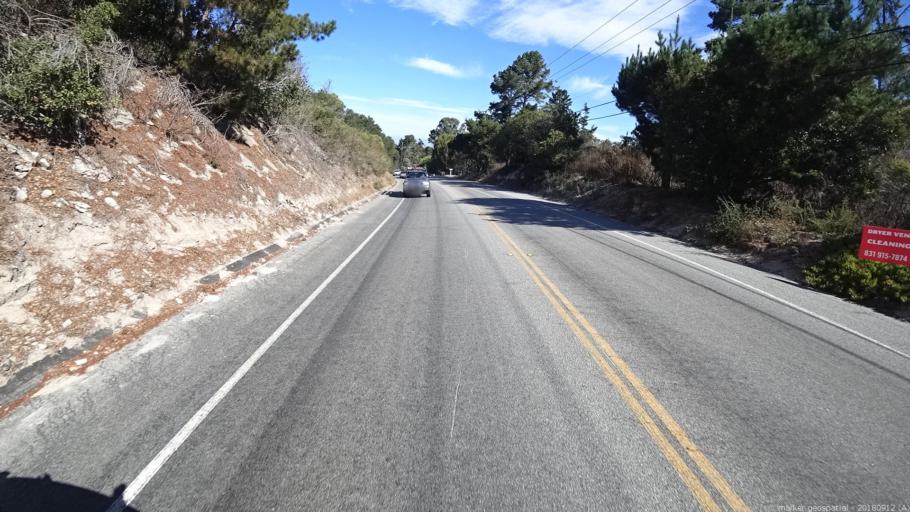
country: US
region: California
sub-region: Monterey County
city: Carmel Valley Village
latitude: 36.5481
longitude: -121.7527
